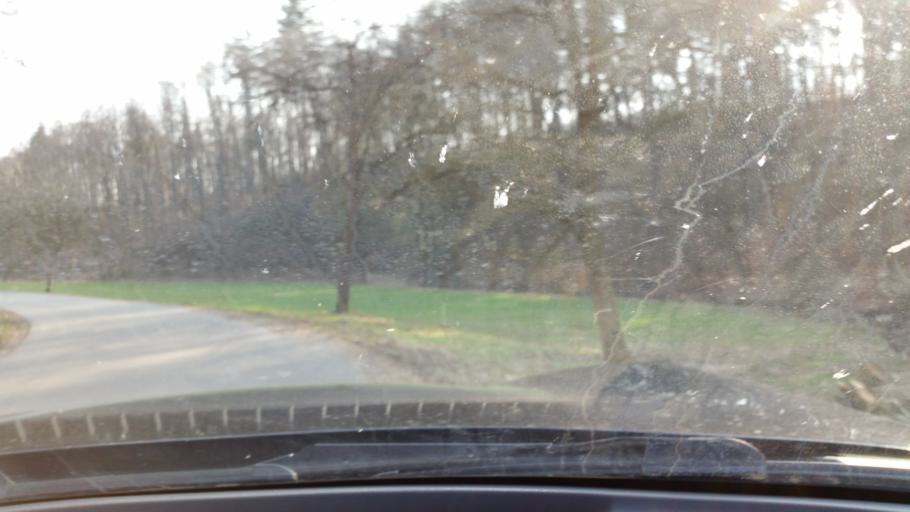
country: DE
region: Baden-Wuerttemberg
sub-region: Regierungsbezirk Stuttgart
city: Mockmuhl
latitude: 49.3437
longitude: 9.3876
